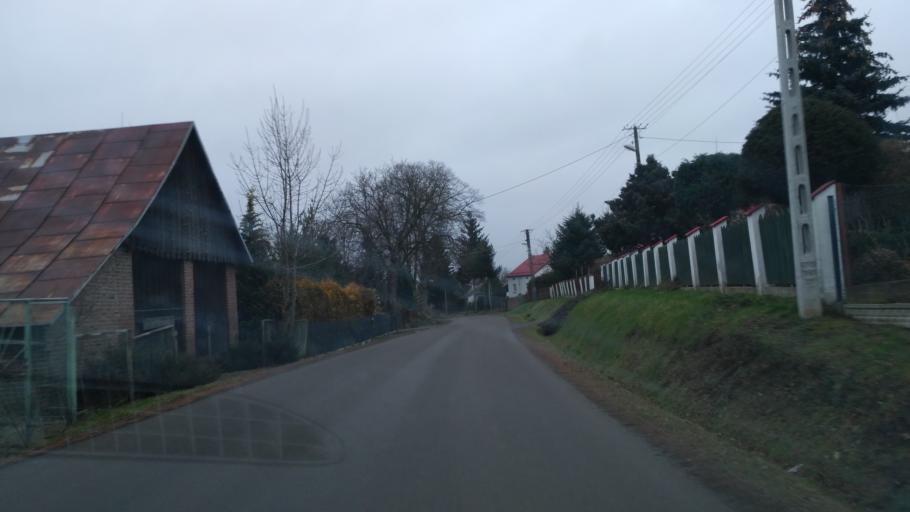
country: PL
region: Subcarpathian Voivodeship
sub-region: Powiat jaroslawski
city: Pruchnik
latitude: 49.9273
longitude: 22.5353
